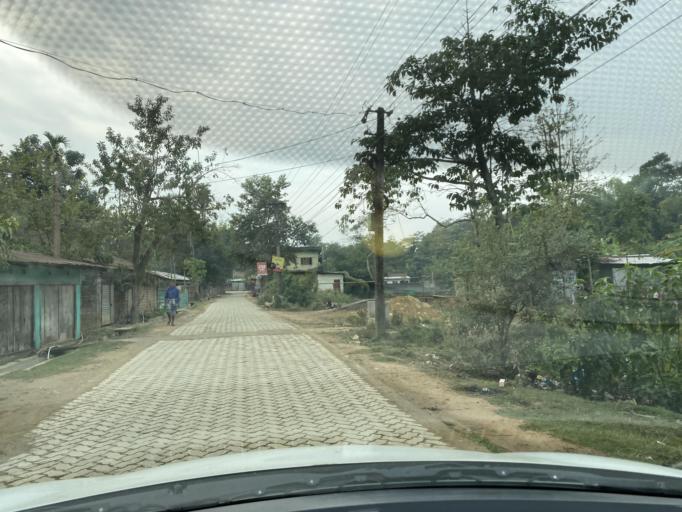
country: IN
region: Assam
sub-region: Cachar
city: Lakhipur
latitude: 24.7886
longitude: 92.9958
